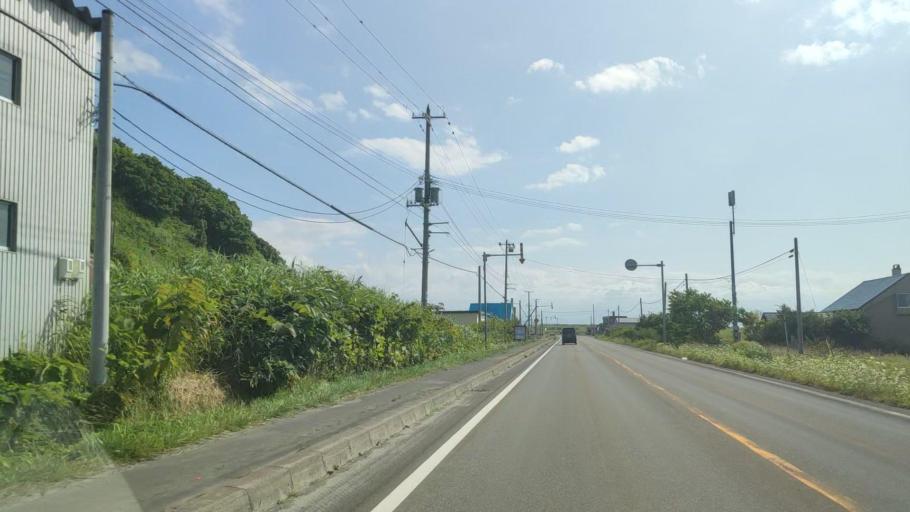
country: JP
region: Hokkaido
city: Rumoi
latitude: 43.9810
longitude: 141.6471
